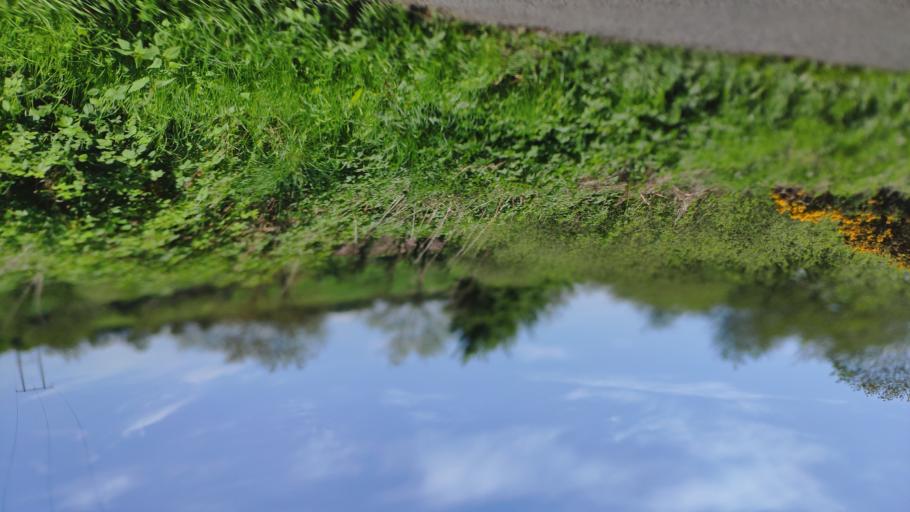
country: IE
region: Munster
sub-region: County Cork
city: Blarney
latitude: 51.9594
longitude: -8.5762
